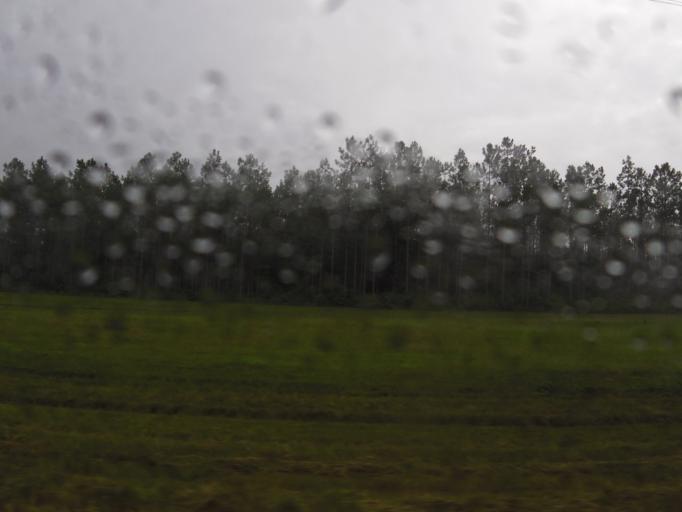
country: US
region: Florida
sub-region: Baker County
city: Macclenny
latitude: 30.3825
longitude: -82.1331
